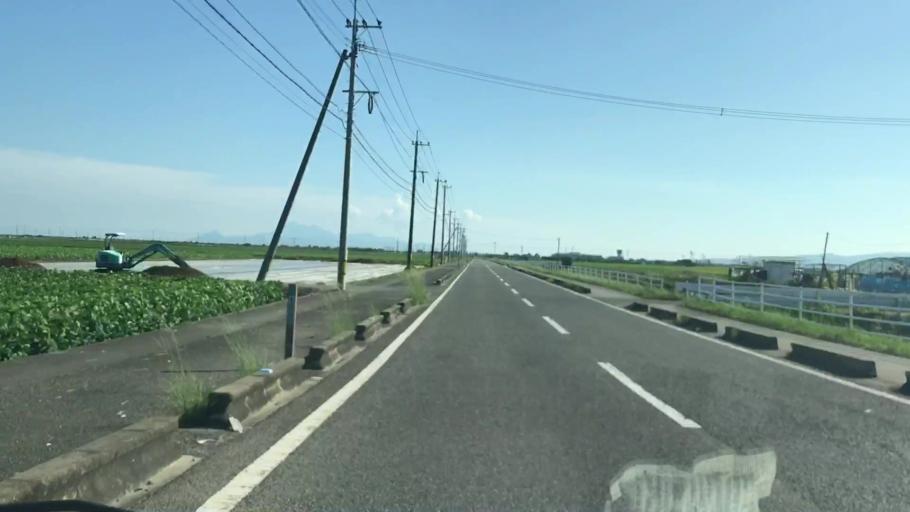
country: JP
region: Saga Prefecture
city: Okawa
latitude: 33.1706
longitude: 130.3104
